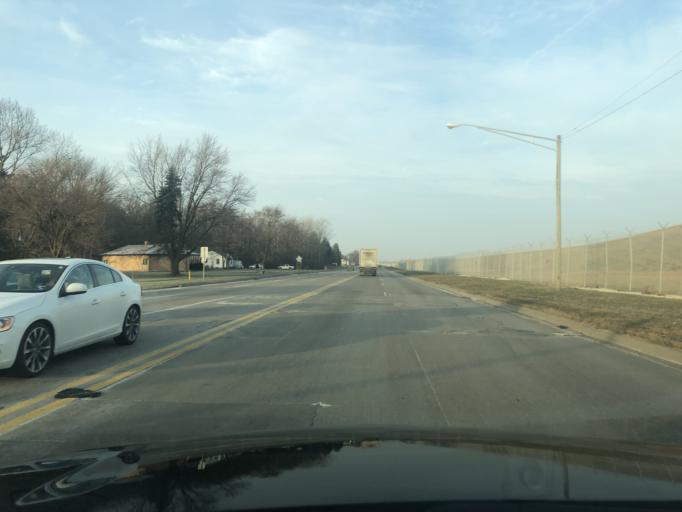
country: US
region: Michigan
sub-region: Wayne County
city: Taylor
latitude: 42.1956
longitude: -83.3262
